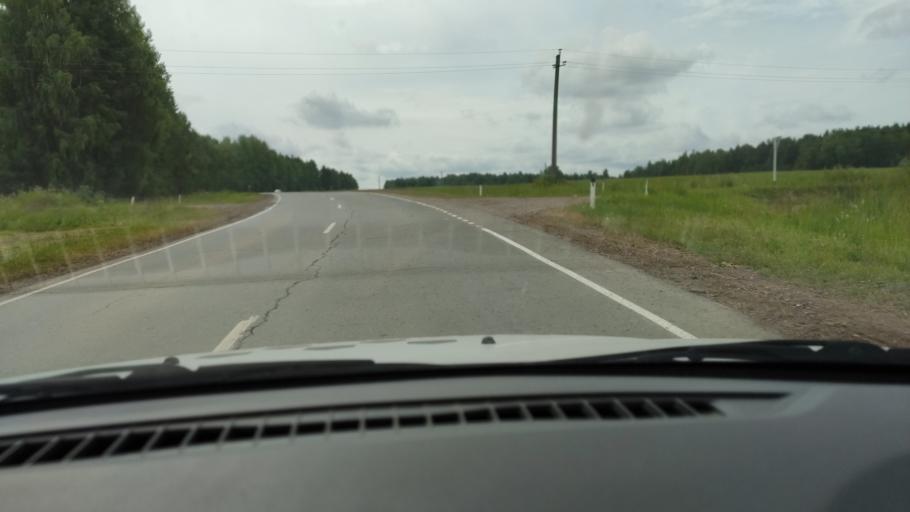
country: RU
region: Perm
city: Kukushtan
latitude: 57.4779
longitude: 56.5798
